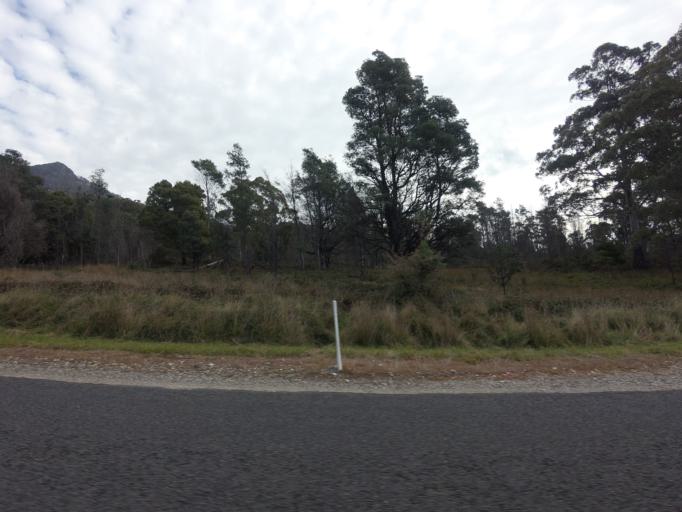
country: AU
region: Tasmania
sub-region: Meander Valley
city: Deloraine
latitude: -41.6346
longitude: 146.7130
